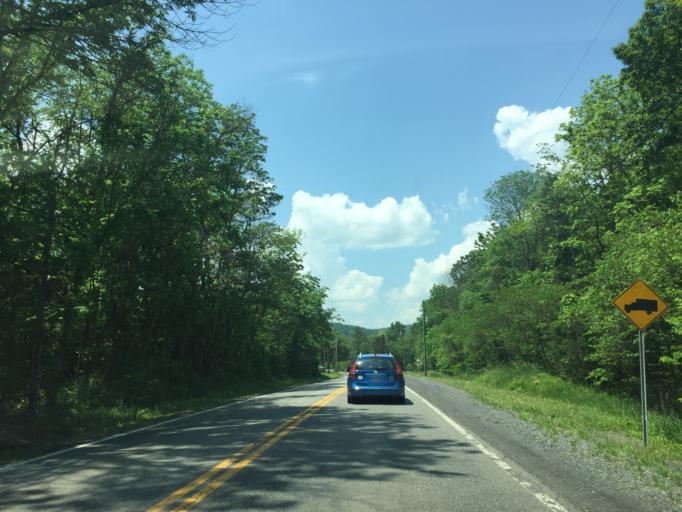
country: US
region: Virginia
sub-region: Shenandoah County
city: Woodstock
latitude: 39.0765
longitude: -78.6112
